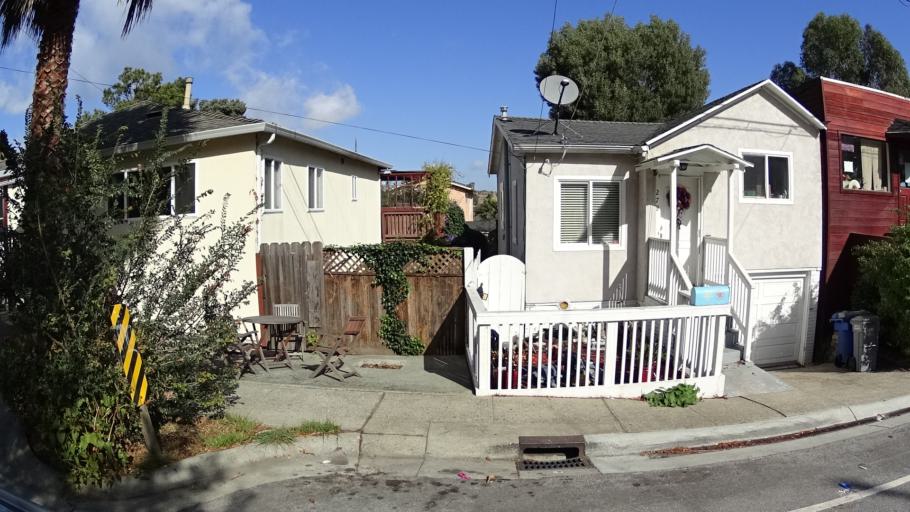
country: US
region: California
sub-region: San Mateo County
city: Brisbane
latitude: 37.6816
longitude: -122.4019
